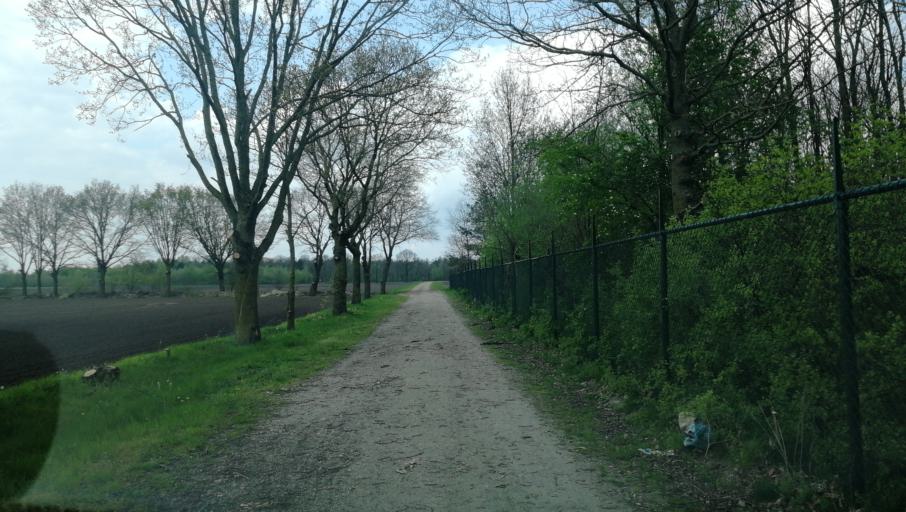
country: NL
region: Limburg
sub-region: Gemeente Peel en Maas
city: Maasbree
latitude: 51.4012
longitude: 5.9826
